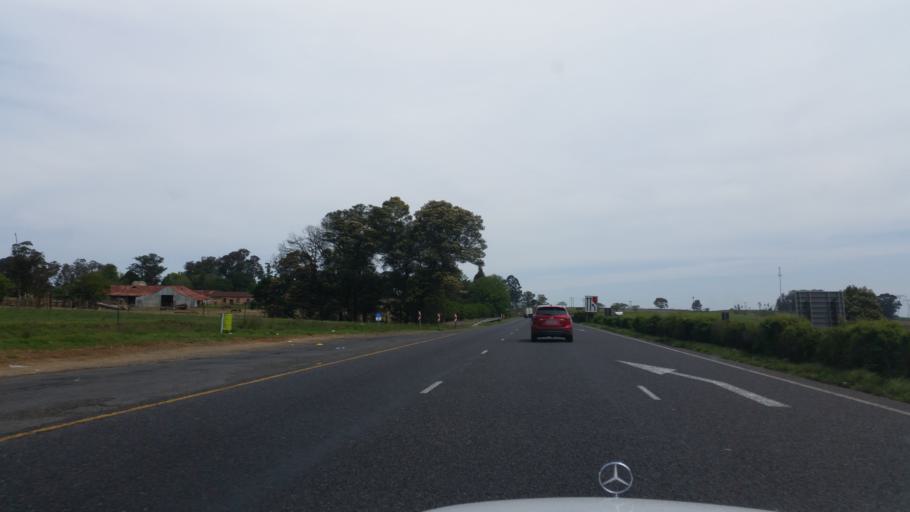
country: ZA
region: KwaZulu-Natal
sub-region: uMgungundlovu District Municipality
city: Howick
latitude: -29.4478
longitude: 30.1781
